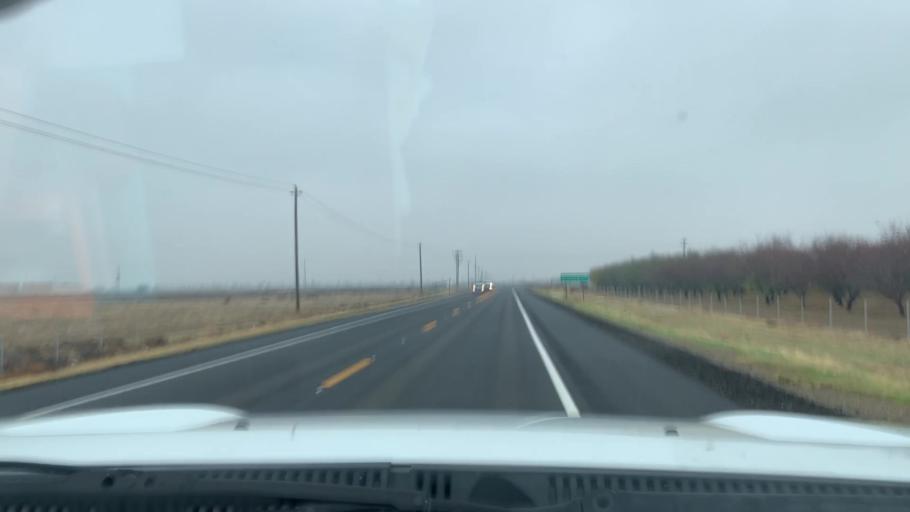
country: US
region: California
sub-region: Kern County
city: Lost Hills
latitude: 35.6157
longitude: -119.7473
